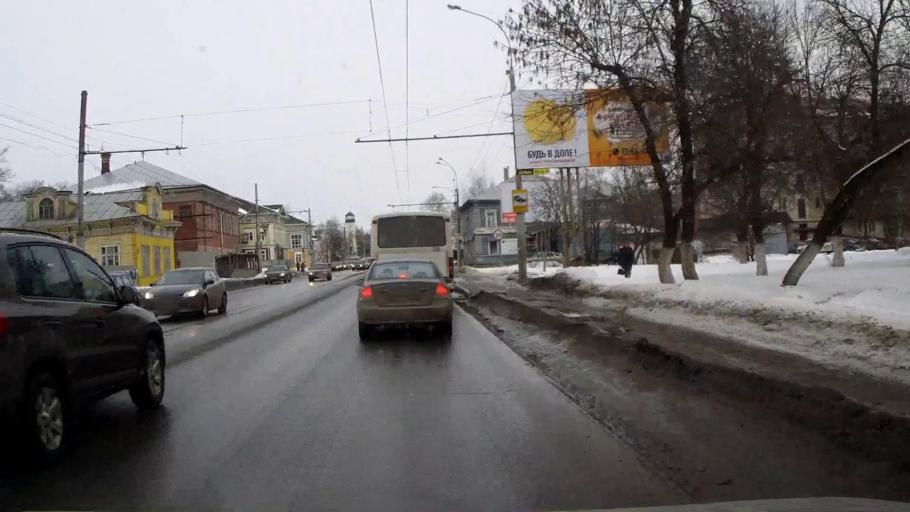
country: RU
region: Vologda
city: Vologda
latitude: 59.2261
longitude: 39.8934
